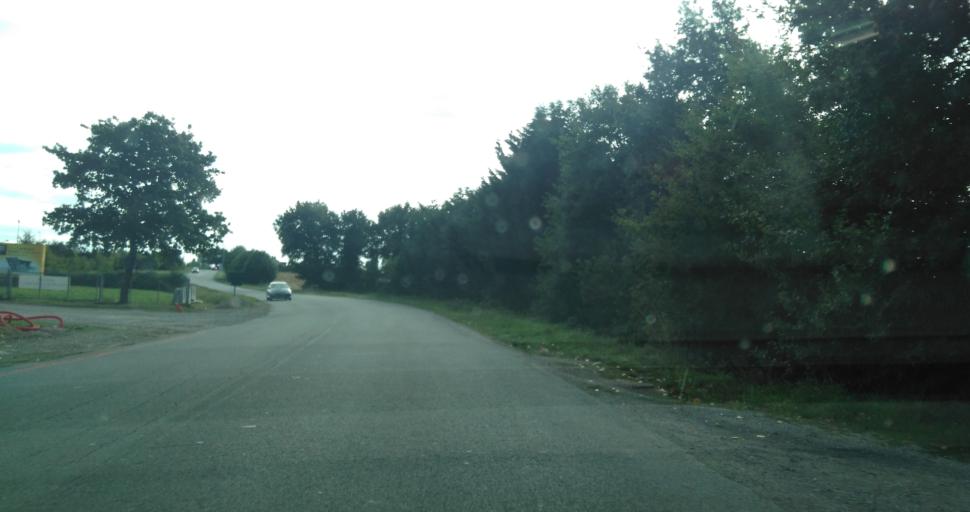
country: FR
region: Brittany
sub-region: Departement d'Ille-et-Vilaine
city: Pleumeleuc
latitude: 48.1775
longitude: -1.9309
